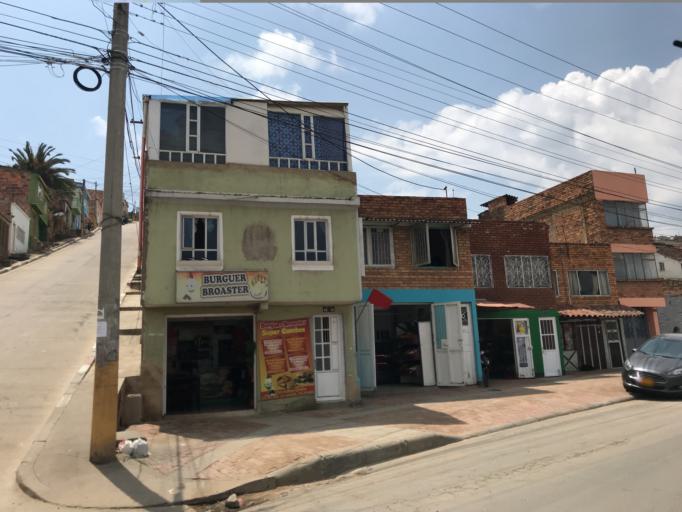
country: CO
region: Boyaca
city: Tunja
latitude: 5.5402
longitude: -73.3681
